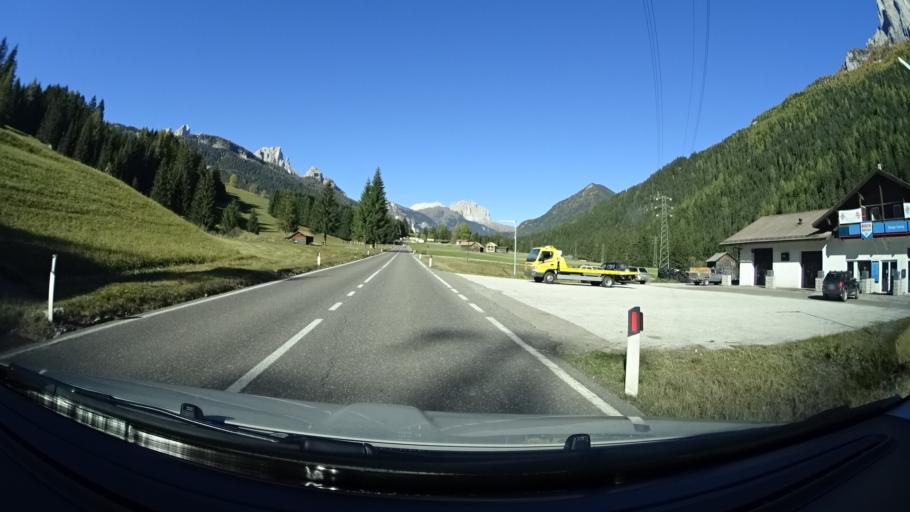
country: IT
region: Trentino-Alto Adige
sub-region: Provincia di Trento
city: Vigo di Fassa
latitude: 46.4095
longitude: 11.6766
